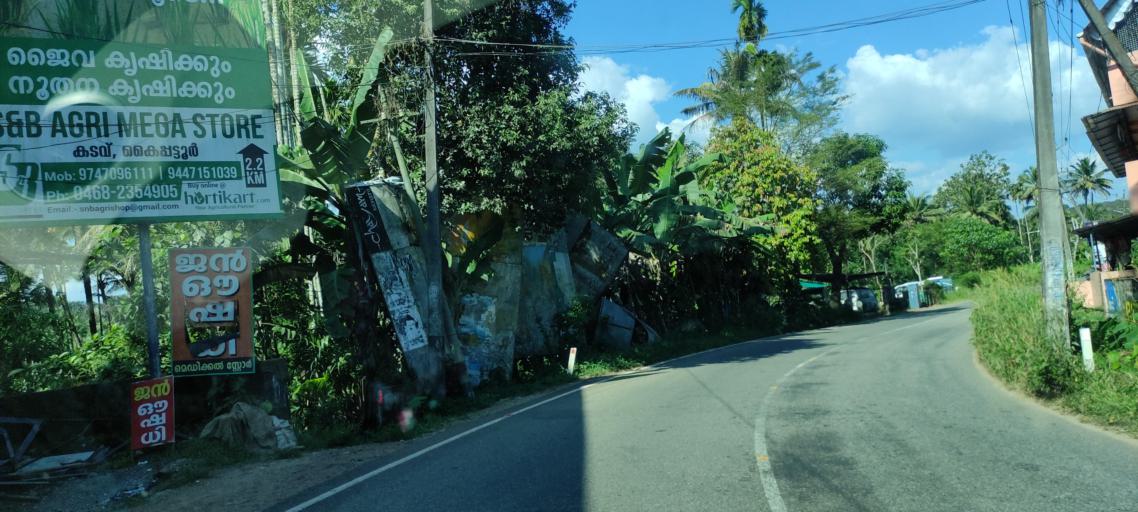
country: IN
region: Kerala
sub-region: Pattanamtitta
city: Adur
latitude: 9.2140
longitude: 76.7465
